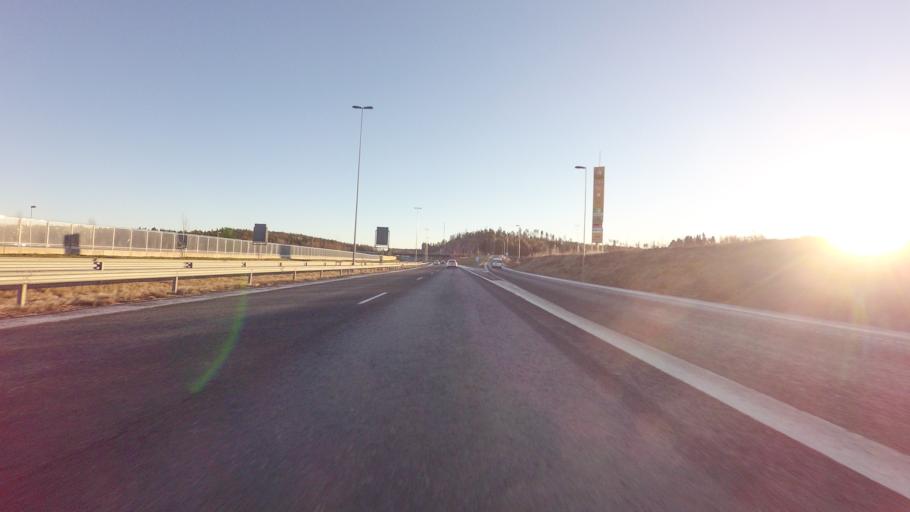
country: FI
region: Uusimaa
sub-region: Helsinki
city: Lohja
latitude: 60.2961
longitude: 24.0614
